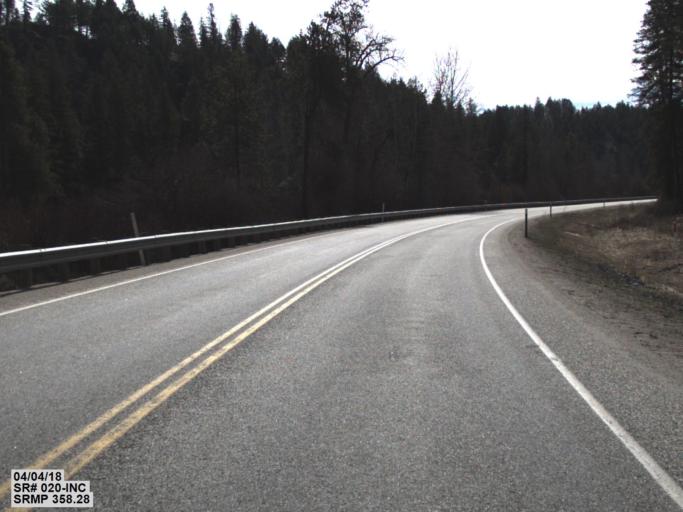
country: US
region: Washington
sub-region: Stevens County
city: Colville
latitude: 48.5385
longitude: -117.8248
